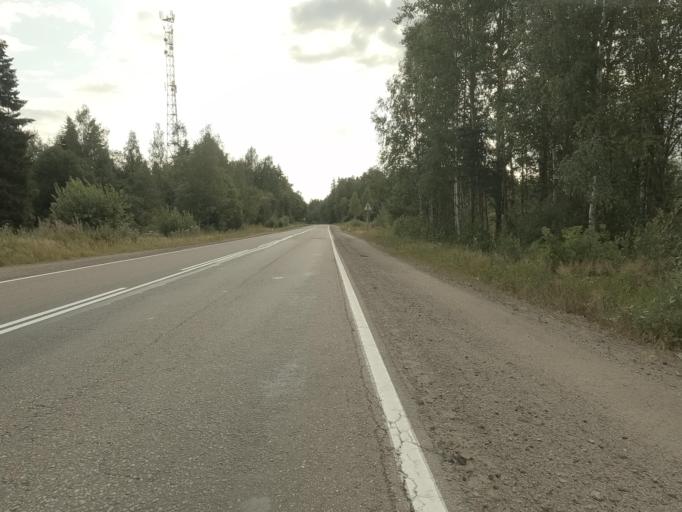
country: RU
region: Leningrad
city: Kamennogorsk
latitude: 60.8781
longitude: 29.0130
